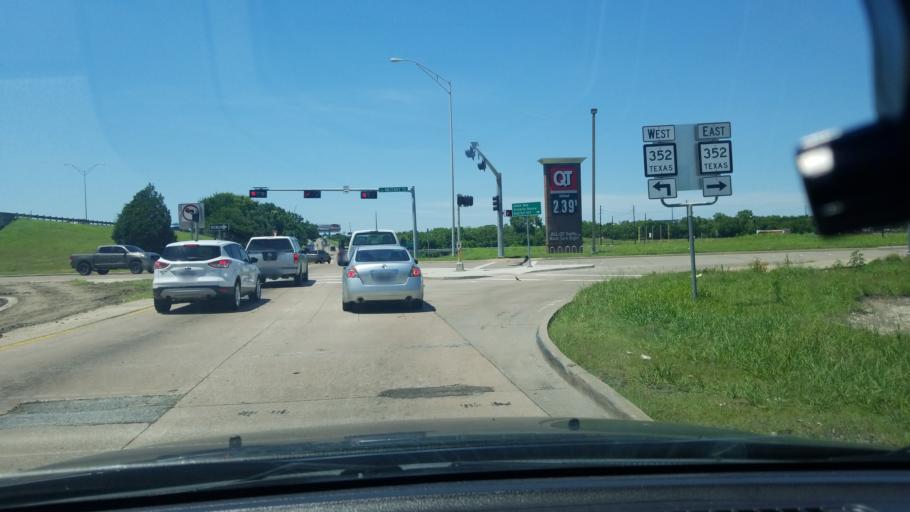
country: US
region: Texas
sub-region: Dallas County
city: Mesquite
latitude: 32.7672
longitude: -96.6214
